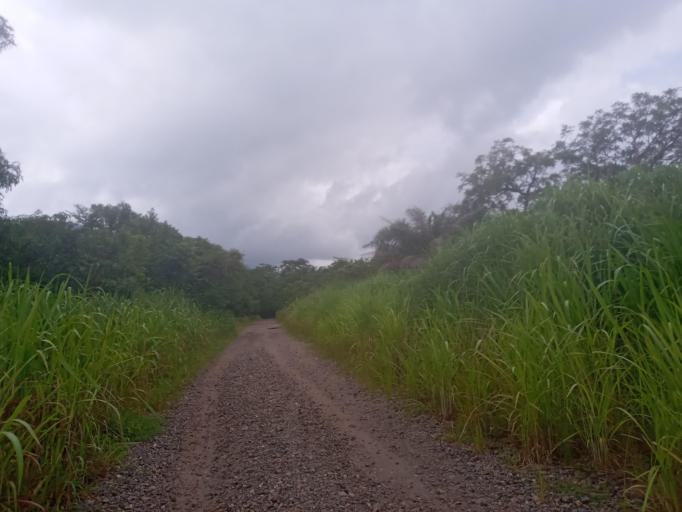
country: SL
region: Northern Province
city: Bumbuna
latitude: 8.9469
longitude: -11.7524
